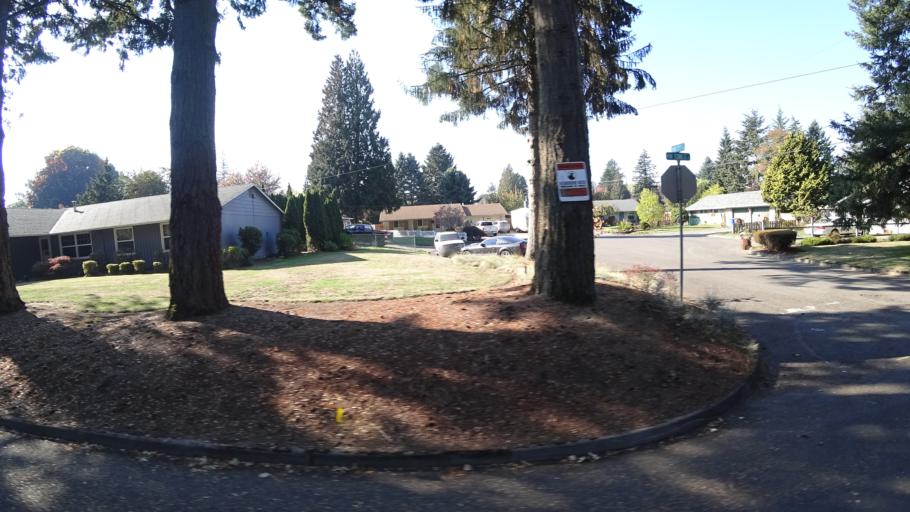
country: US
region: Oregon
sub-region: Multnomah County
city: Gresham
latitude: 45.5025
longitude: -122.4474
